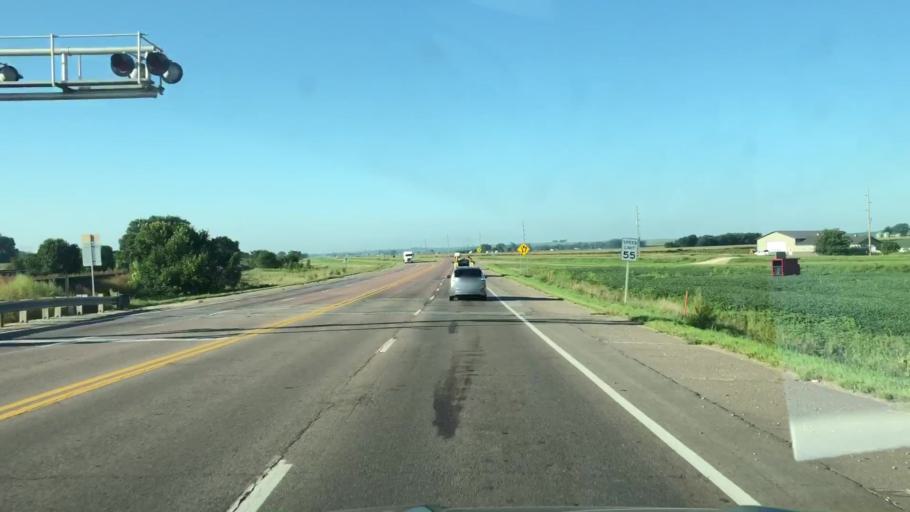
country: US
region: Iowa
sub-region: Plymouth County
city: Le Mars
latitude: 42.7149
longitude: -96.2493
